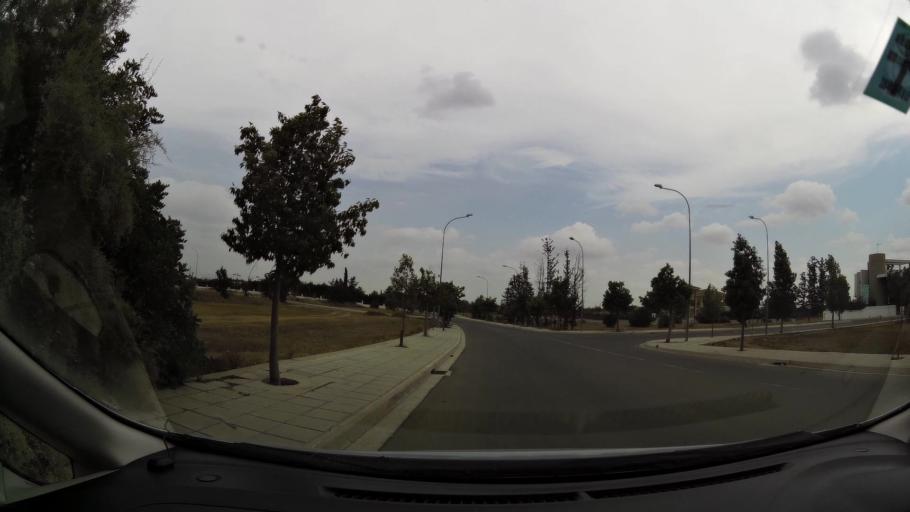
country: CY
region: Lefkosia
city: Geri
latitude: 35.0782
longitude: 33.3833
